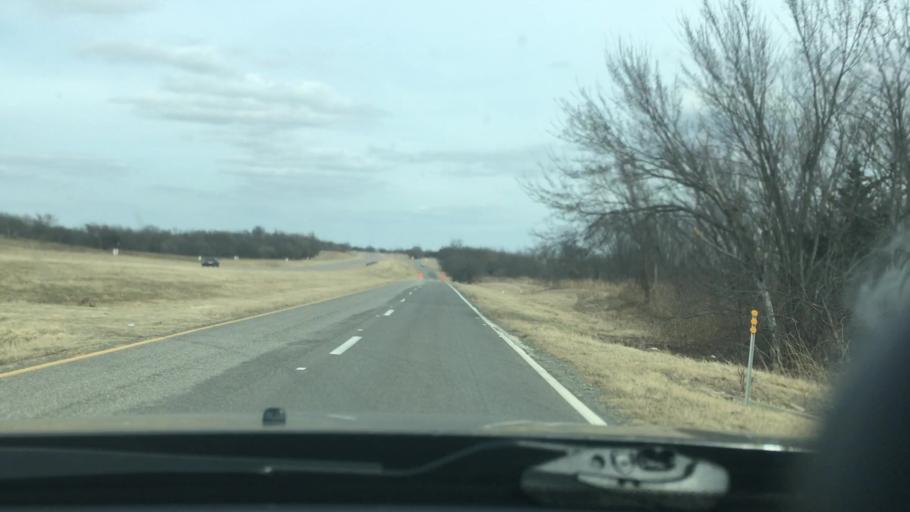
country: US
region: Oklahoma
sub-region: Pontotoc County
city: Ada
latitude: 34.6951
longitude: -96.7393
